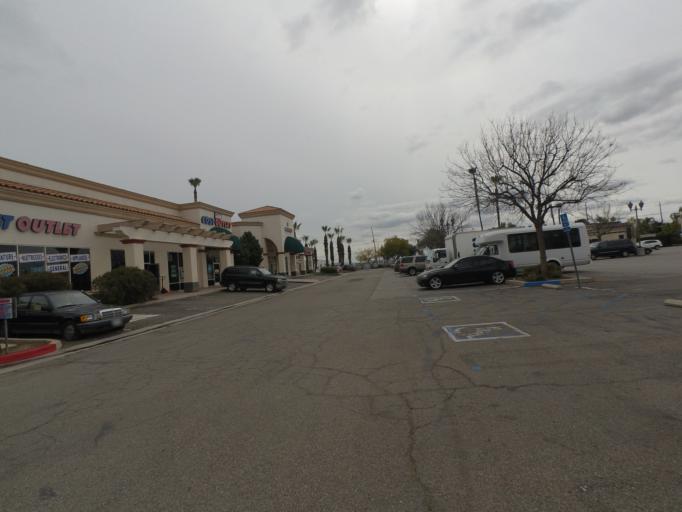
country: US
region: California
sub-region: Riverside County
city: March Air Force Base
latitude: 33.9184
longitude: -117.2597
